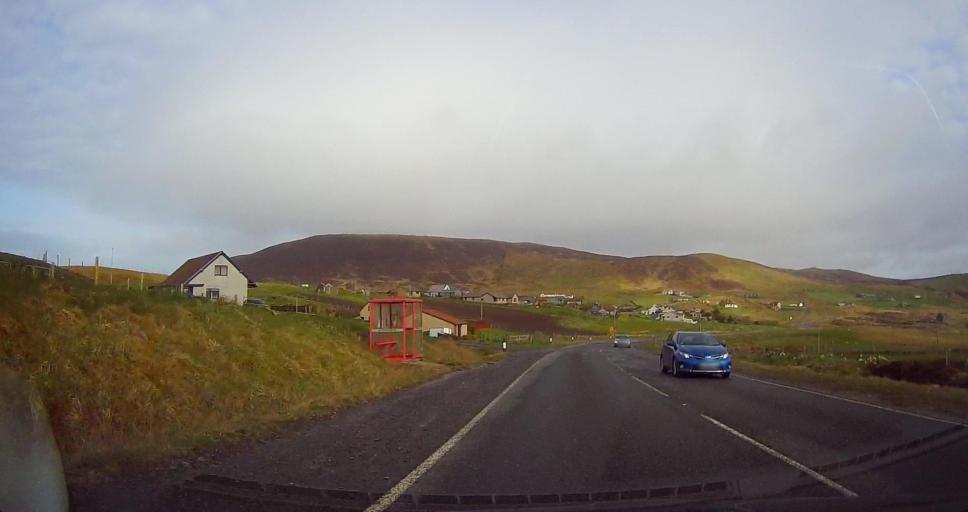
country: GB
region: Scotland
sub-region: Shetland Islands
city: Sandwick
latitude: 60.0952
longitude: -1.2316
